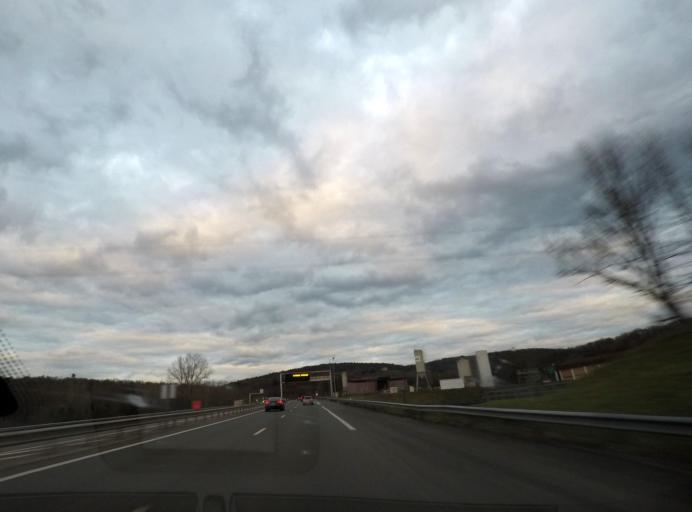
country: FR
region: Rhone-Alpes
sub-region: Departement de l'Ain
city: Poncin
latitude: 46.0944
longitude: 5.4176
